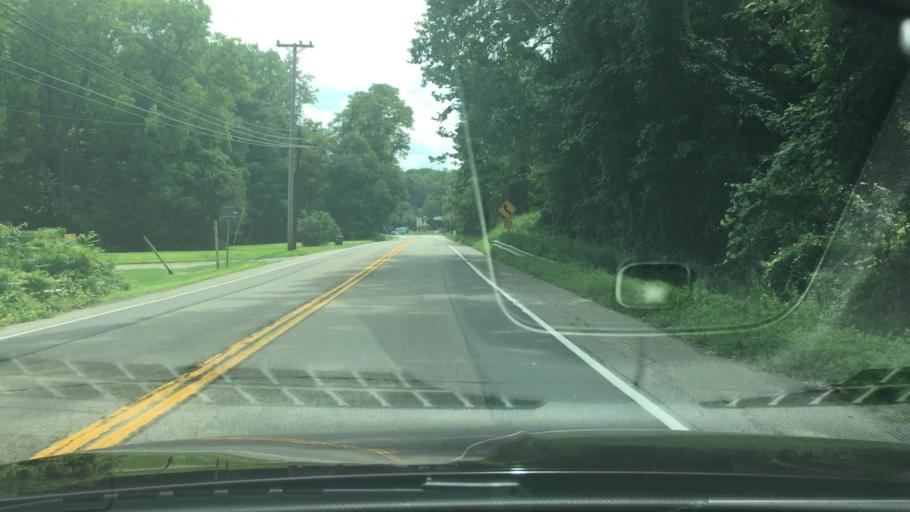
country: US
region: New York
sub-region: Dutchess County
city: Hillside Lake
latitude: 41.5540
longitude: -73.8016
